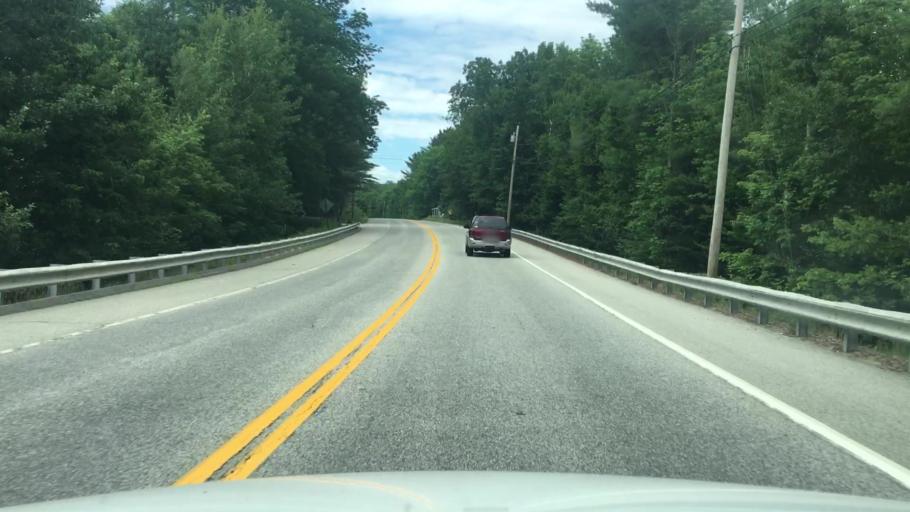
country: US
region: Maine
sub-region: Oxford County
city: West Paris
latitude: 44.3548
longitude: -70.5637
